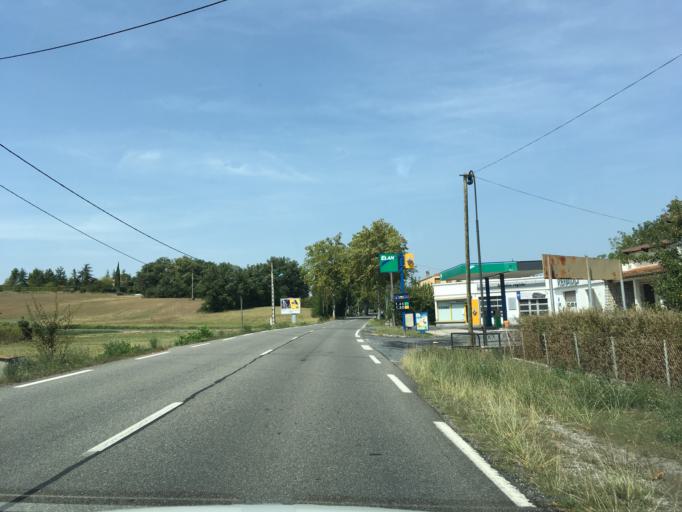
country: FR
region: Midi-Pyrenees
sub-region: Departement du Tarn
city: Castres
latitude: 43.6304
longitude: 2.2275
